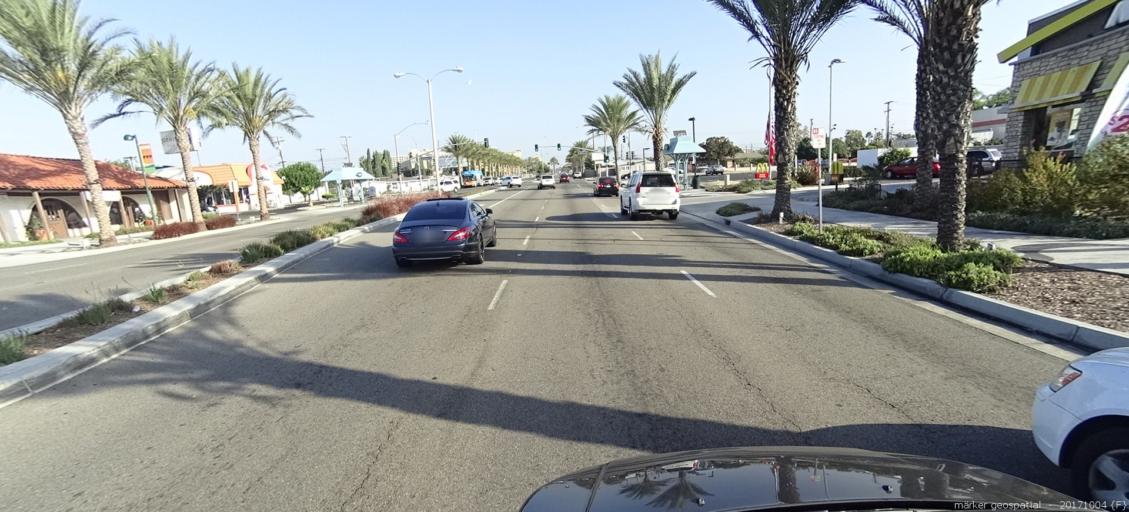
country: US
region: California
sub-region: Orange County
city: Garden Grove
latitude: 33.7807
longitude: -117.9148
